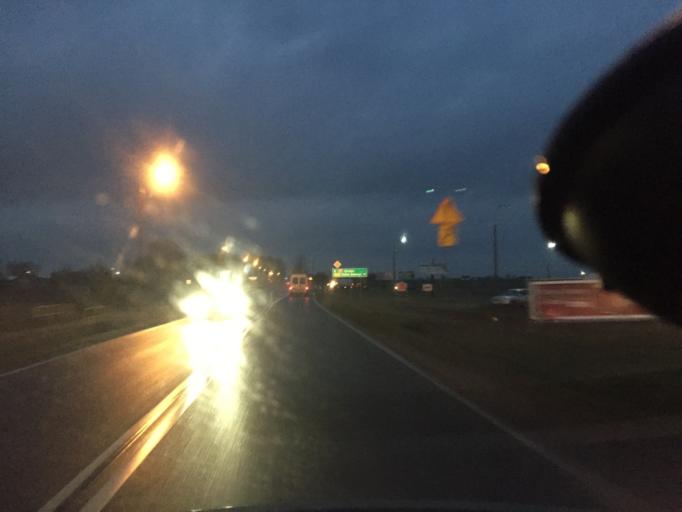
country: PL
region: Kujawsko-Pomorskie
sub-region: Powiat golubsko-dobrzynski
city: Kowalewo Pomorskie
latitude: 53.1612
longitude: 18.9162
